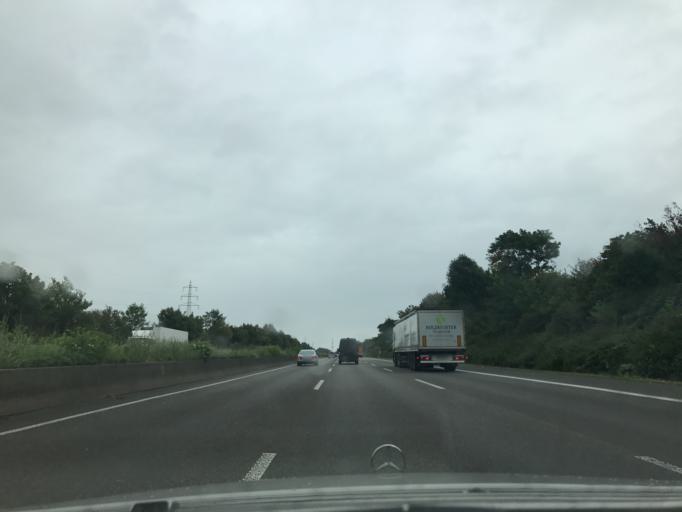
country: DE
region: North Rhine-Westphalia
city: Haan
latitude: 51.2023
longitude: 7.0033
